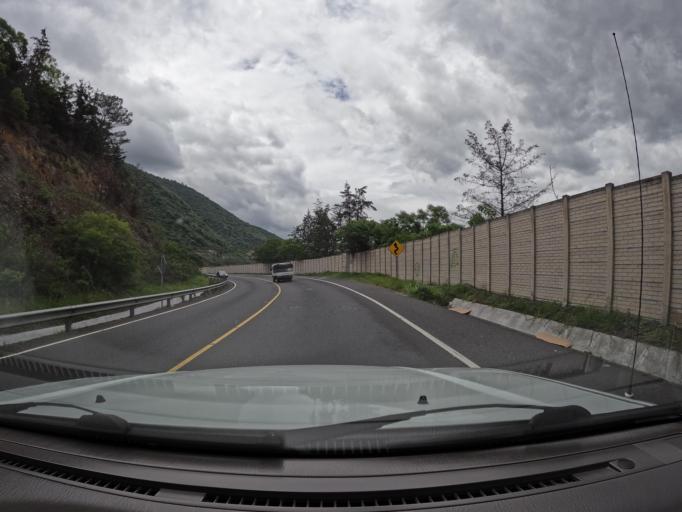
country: GT
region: Sacatepequez
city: San Antonio Aguas Calientes
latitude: 14.5477
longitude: -90.7592
